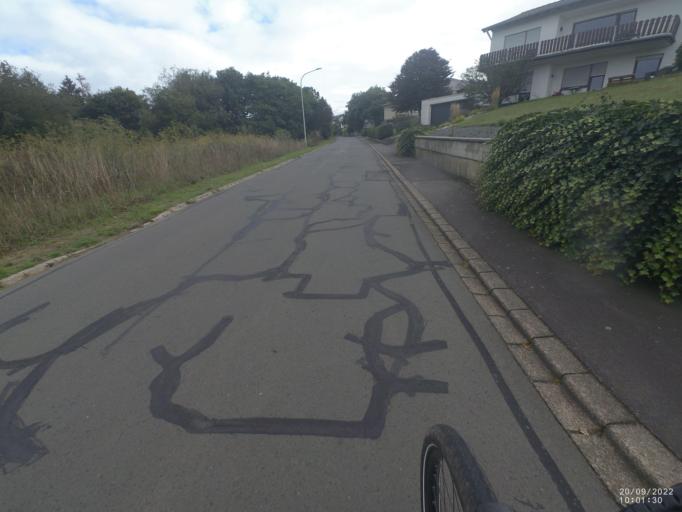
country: DE
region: Rheinland-Pfalz
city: Saxler
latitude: 50.1319
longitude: 6.8986
